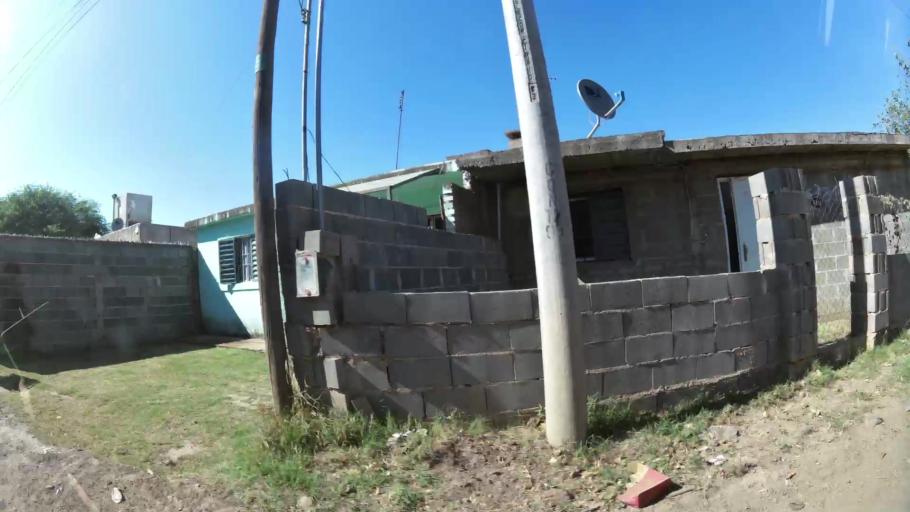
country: AR
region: Cordoba
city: Villa Allende
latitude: -31.3220
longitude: -64.2454
